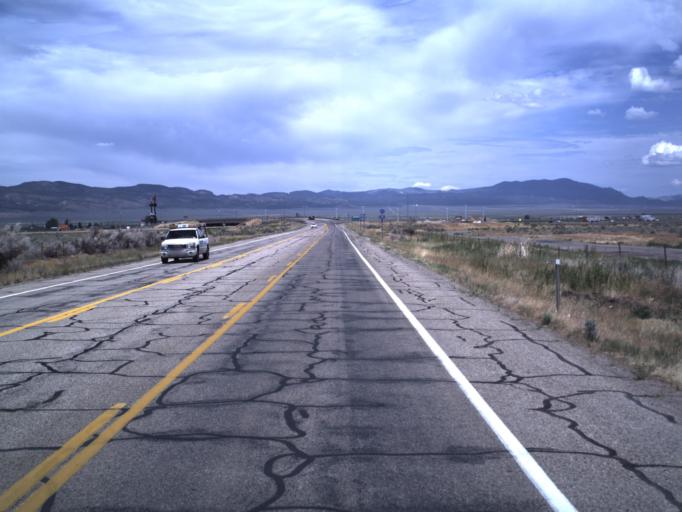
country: US
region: Utah
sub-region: Iron County
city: Parowan
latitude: 37.8539
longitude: -112.8278
